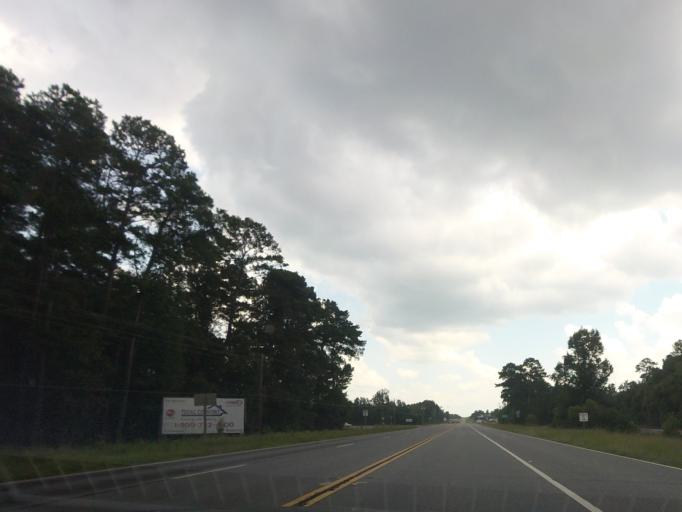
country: US
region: Georgia
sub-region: Bleckley County
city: Cochran
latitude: 32.4215
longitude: -83.3587
